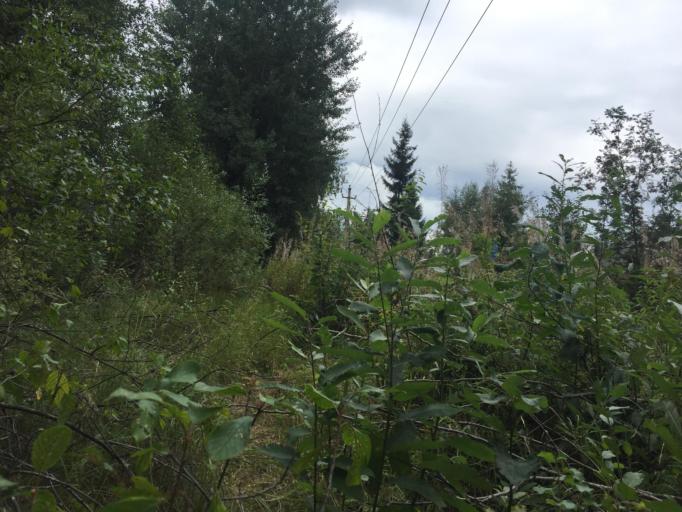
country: RU
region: Leningrad
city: Rozhdestveno
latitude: 59.2949
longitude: 30.0127
